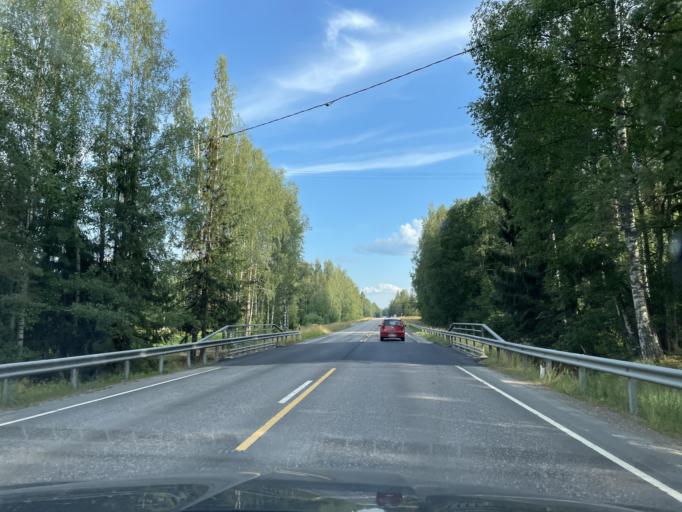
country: FI
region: Paijanne Tavastia
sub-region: Lahti
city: Padasjoki
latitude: 61.3602
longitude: 25.2228
